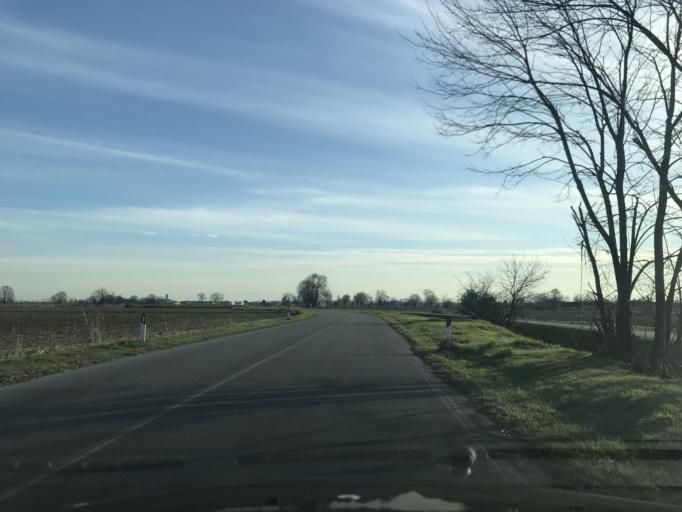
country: IT
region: Lombardy
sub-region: Provincia di Lodi
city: Bargano
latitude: 45.2536
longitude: 9.4343
